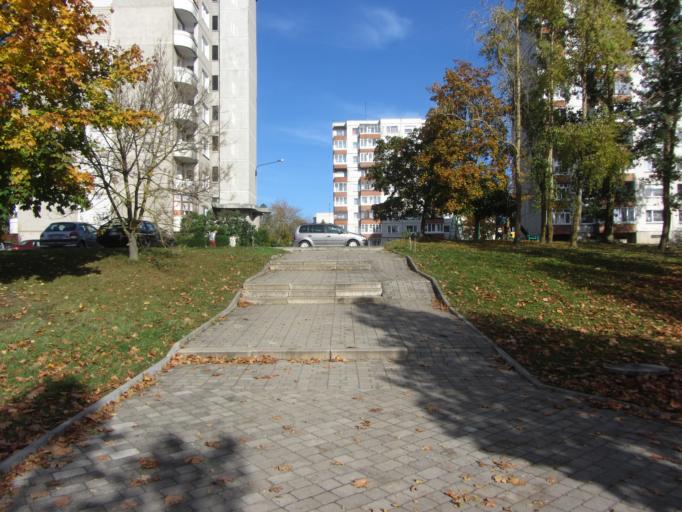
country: LT
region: Vilnius County
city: Elektrenai
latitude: 54.7854
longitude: 24.6694
